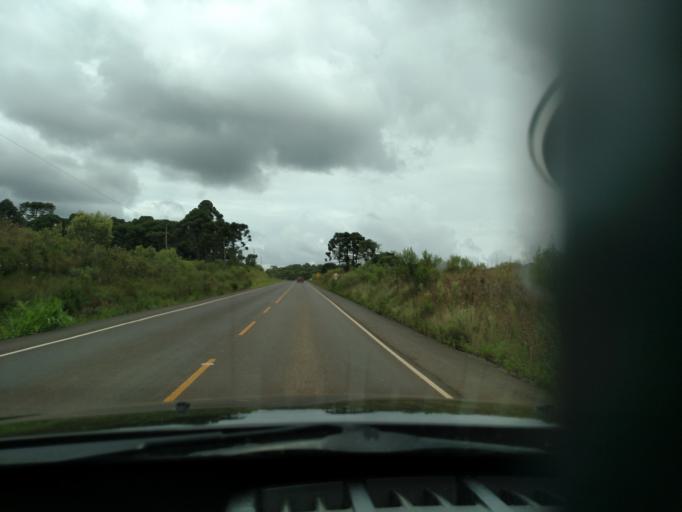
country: BR
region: Rio Grande do Sul
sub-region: Vacaria
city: Estrela
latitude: -27.9217
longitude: -50.6479
